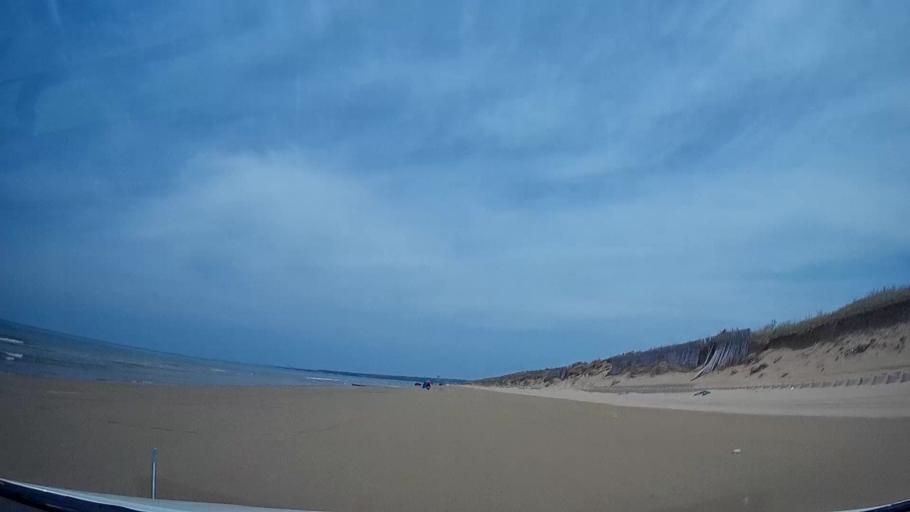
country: JP
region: Ishikawa
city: Hakui
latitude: 36.8647
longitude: 136.7581
